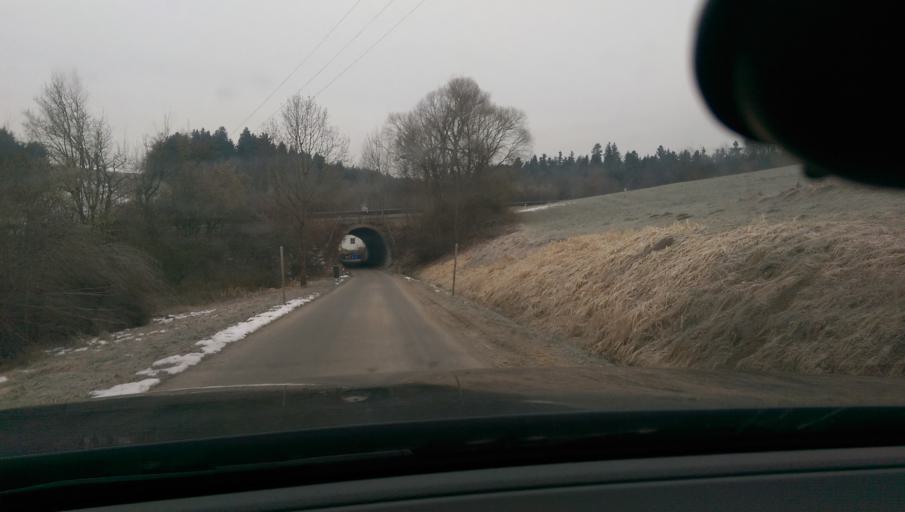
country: DE
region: Bavaria
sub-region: Lower Bavaria
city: Hutthurm
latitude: 48.6626
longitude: 13.4813
